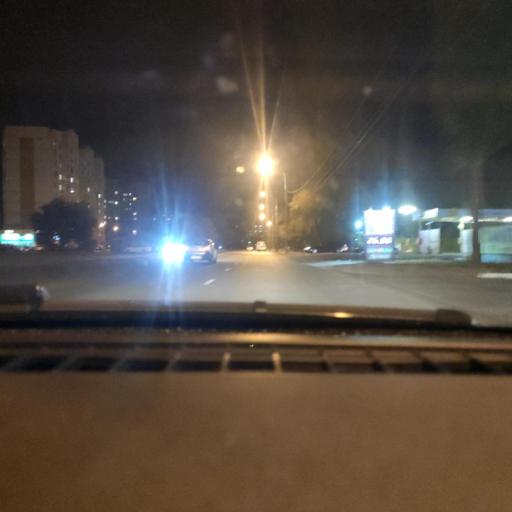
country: RU
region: Voronezj
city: Voronezh
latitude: 51.6461
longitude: 39.2673
